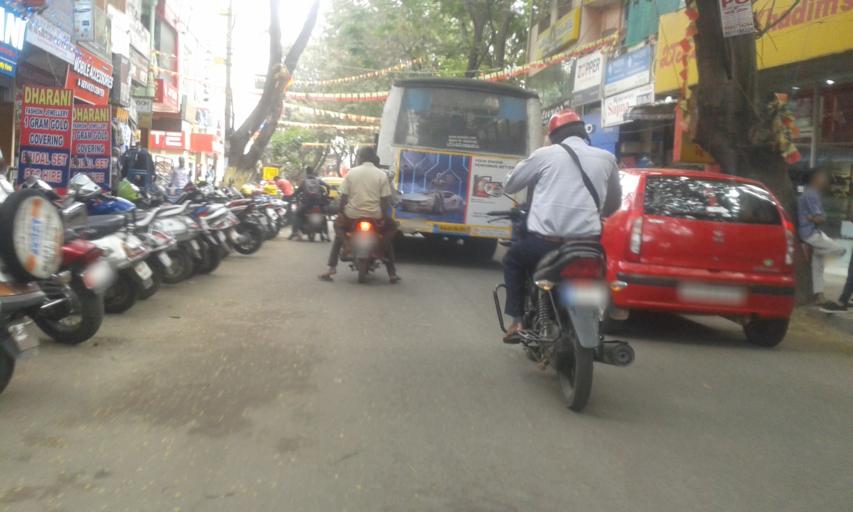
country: IN
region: Karnataka
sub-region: Bangalore Urban
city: Bangalore
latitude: 12.9724
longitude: 77.6515
